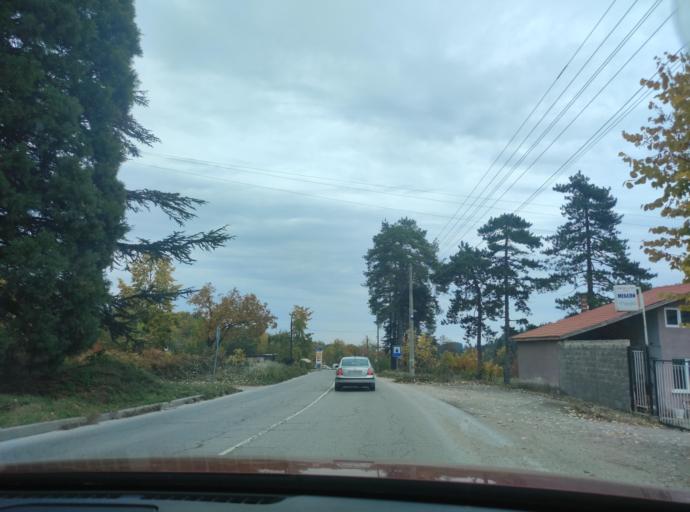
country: BG
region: Montana
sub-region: Obshtina Berkovitsa
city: Berkovitsa
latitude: 43.1870
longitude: 23.1577
